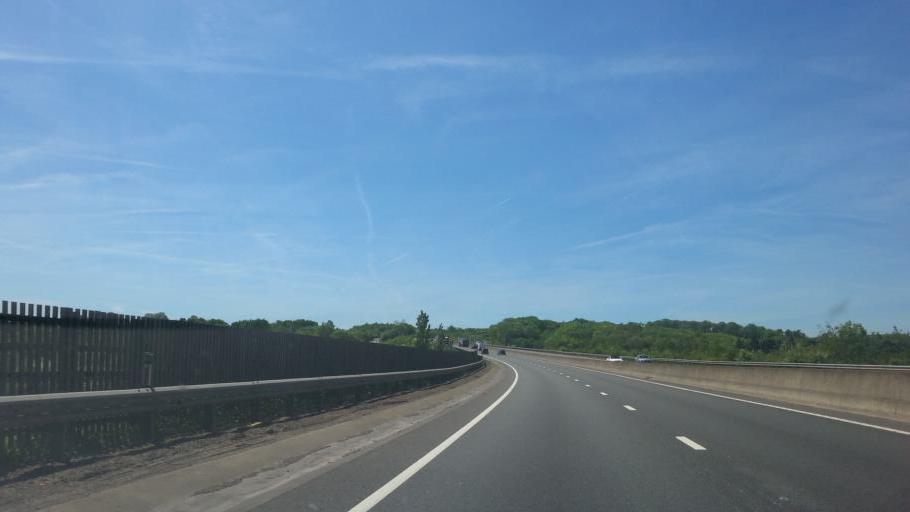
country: GB
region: England
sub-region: Central Bedfordshire
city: Lidlington
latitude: 52.0469
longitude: -0.5871
